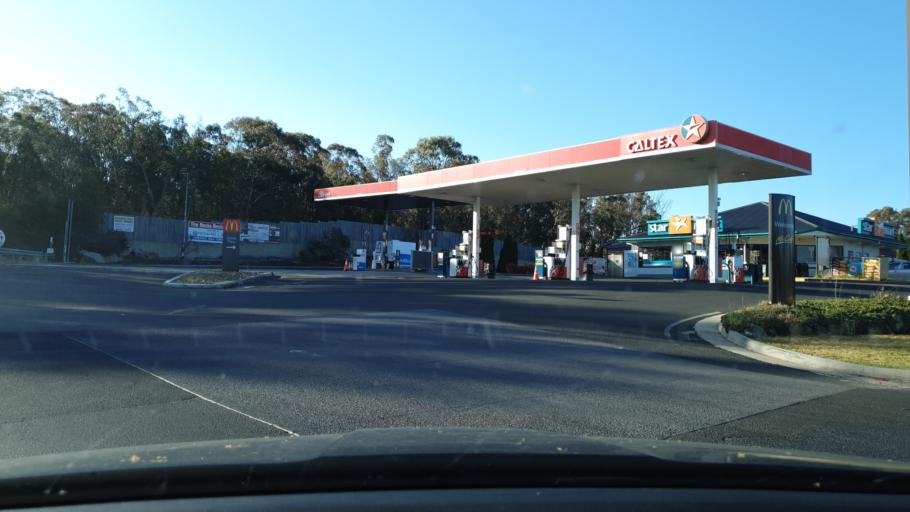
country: AU
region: Queensland
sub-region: Southern Downs
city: Stanthorpe
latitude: -28.6316
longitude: 151.9539
